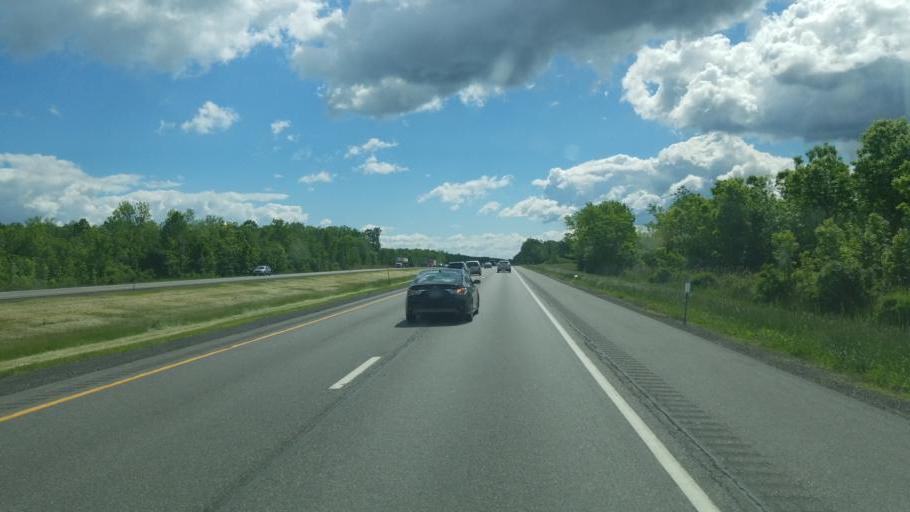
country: US
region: New York
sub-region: Madison County
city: Chittenango
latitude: 43.0937
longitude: -75.8257
